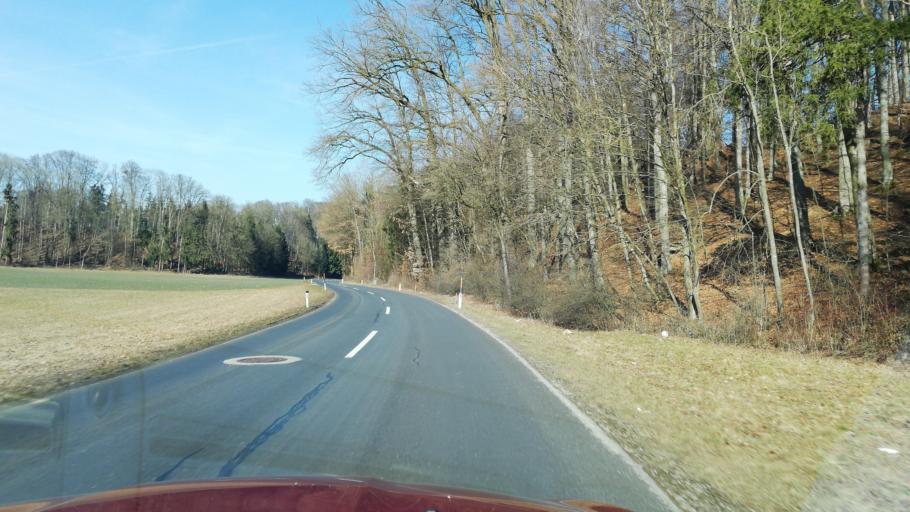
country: AT
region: Upper Austria
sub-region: Politischer Bezirk Vocklabruck
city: Desselbrunn
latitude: 48.0272
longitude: 13.7749
